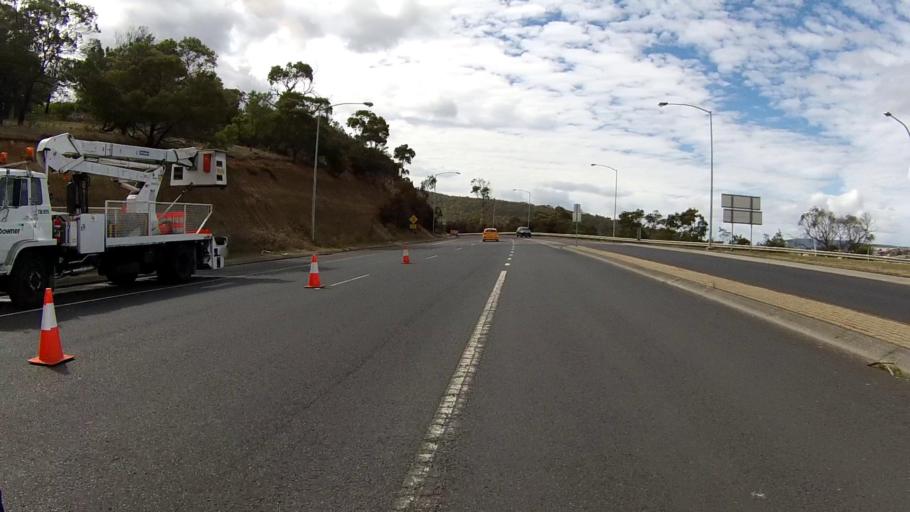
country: AU
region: Tasmania
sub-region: Glenorchy
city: Lutana
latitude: -42.8142
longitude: 147.3153
